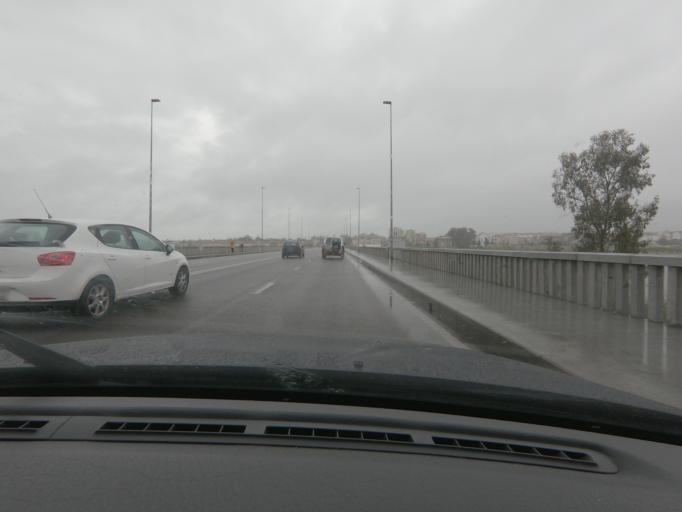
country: ES
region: Extremadura
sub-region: Provincia de Badajoz
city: Badajoz
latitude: 38.8789
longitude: -6.9810
